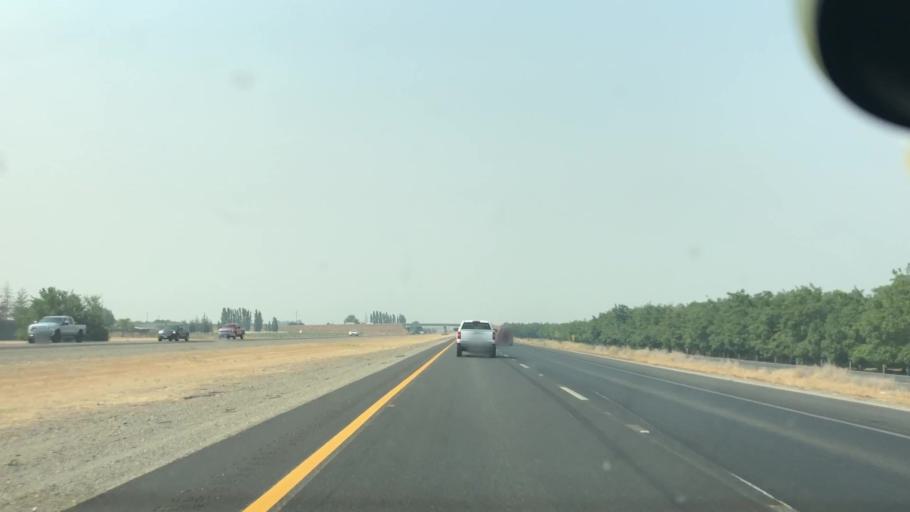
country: US
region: California
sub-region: San Joaquin County
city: Tracy
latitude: 37.6618
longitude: -121.3430
